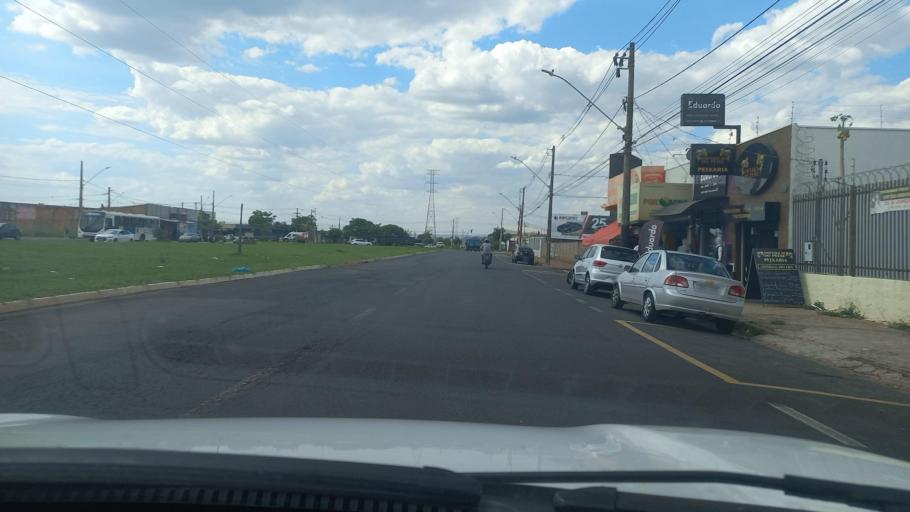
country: BR
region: Minas Gerais
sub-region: Uberaba
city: Uberaba
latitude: -19.7564
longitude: -47.9889
